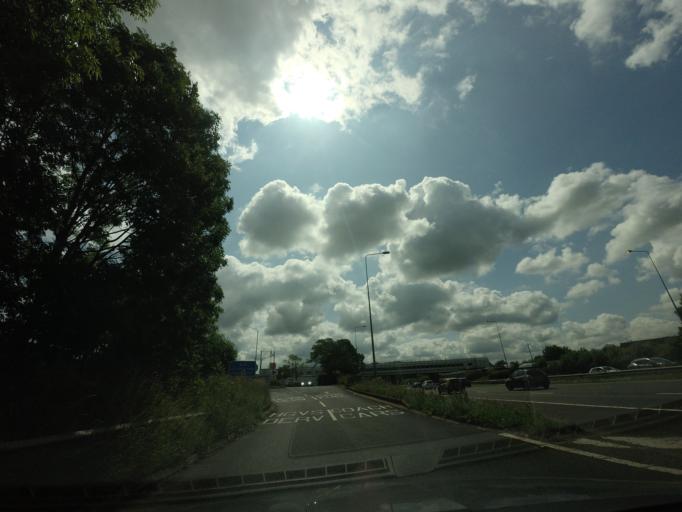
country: GB
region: England
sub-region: Lancashire
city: Coppull
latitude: 53.6327
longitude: -2.6908
